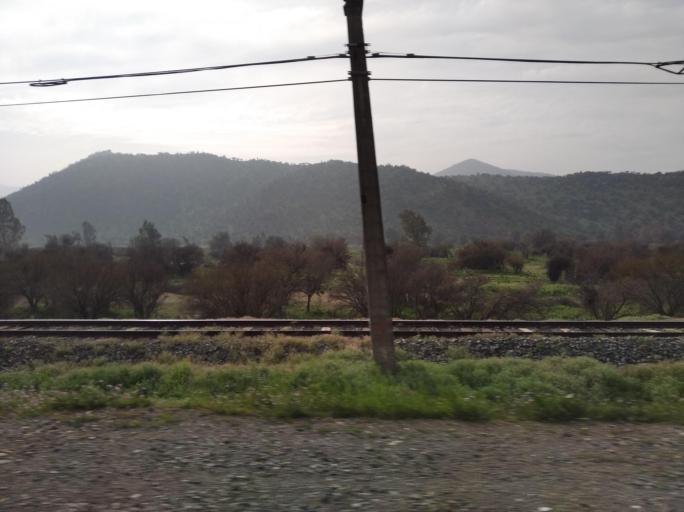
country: CL
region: Santiago Metropolitan
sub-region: Provincia de Chacabuco
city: Lampa
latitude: -33.1407
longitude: -70.9165
